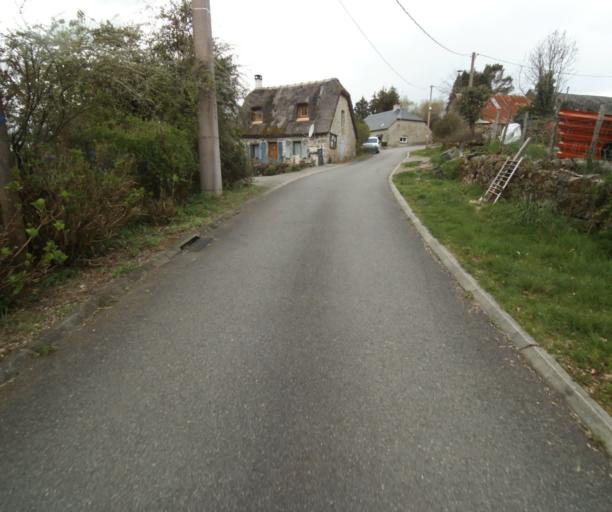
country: FR
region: Limousin
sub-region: Departement de la Correze
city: Correze
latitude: 45.2955
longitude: 1.9200
